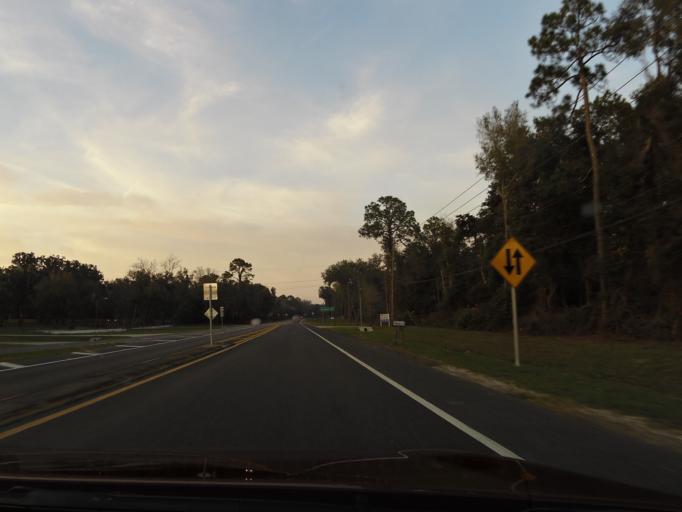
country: US
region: Florida
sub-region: Volusia County
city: North DeLand
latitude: 29.1040
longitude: -81.2949
